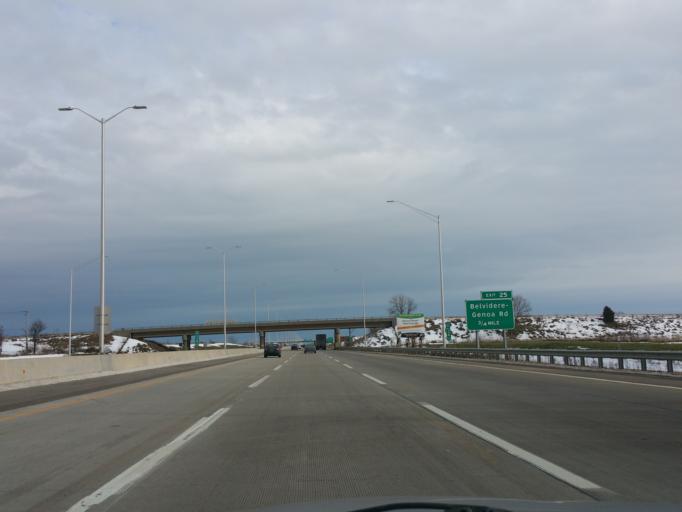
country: US
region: Illinois
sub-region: Boone County
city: Belvidere
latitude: 42.2335
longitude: -88.8296
